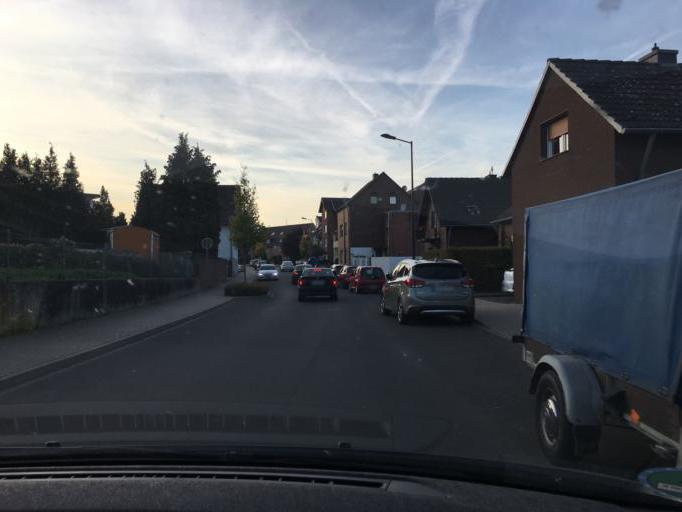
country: DE
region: North Rhine-Westphalia
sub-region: Regierungsbezirk Koln
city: Hurth
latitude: 50.8658
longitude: 6.8855
